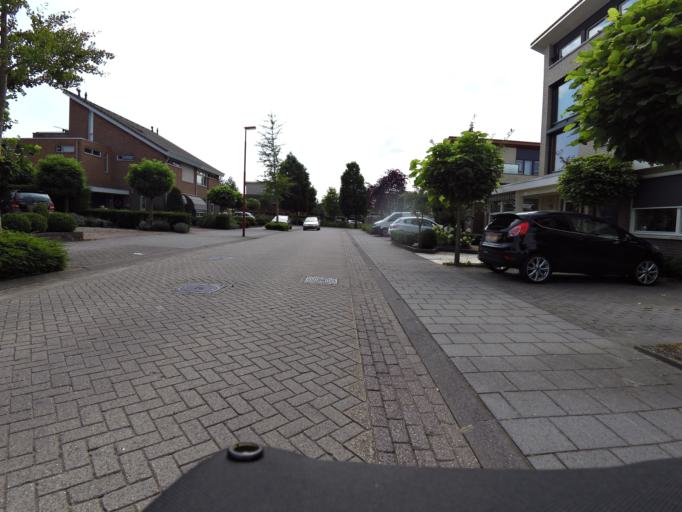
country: NL
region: South Holland
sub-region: Gemeente Oud-Beijerland
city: Oud-Beijerland
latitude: 51.8156
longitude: 4.4367
